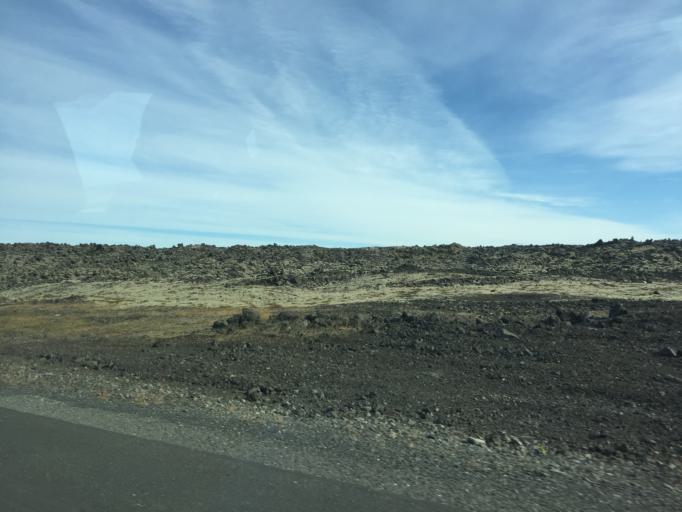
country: IS
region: Capital Region
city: Alftanes
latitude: 64.0126
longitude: -22.1823
